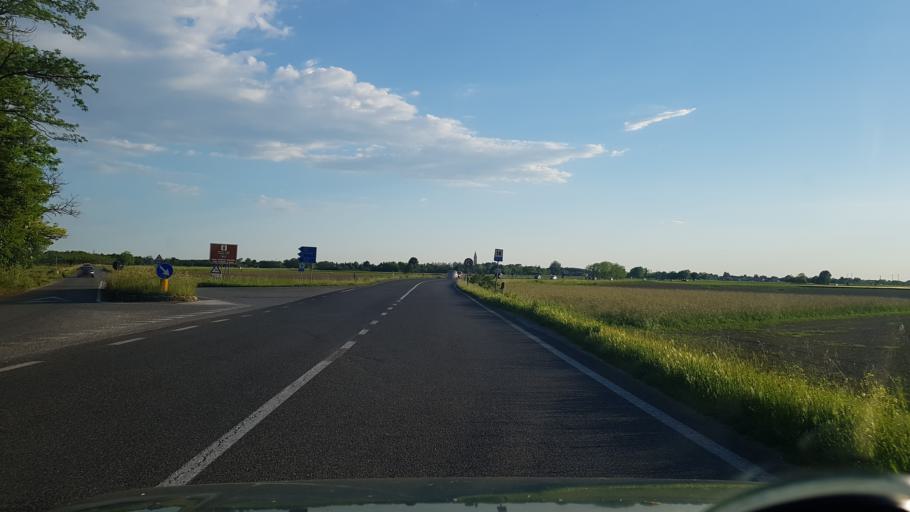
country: IT
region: Friuli Venezia Giulia
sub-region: Provincia di Udine
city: Ruda
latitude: 45.8492
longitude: 13.4166
